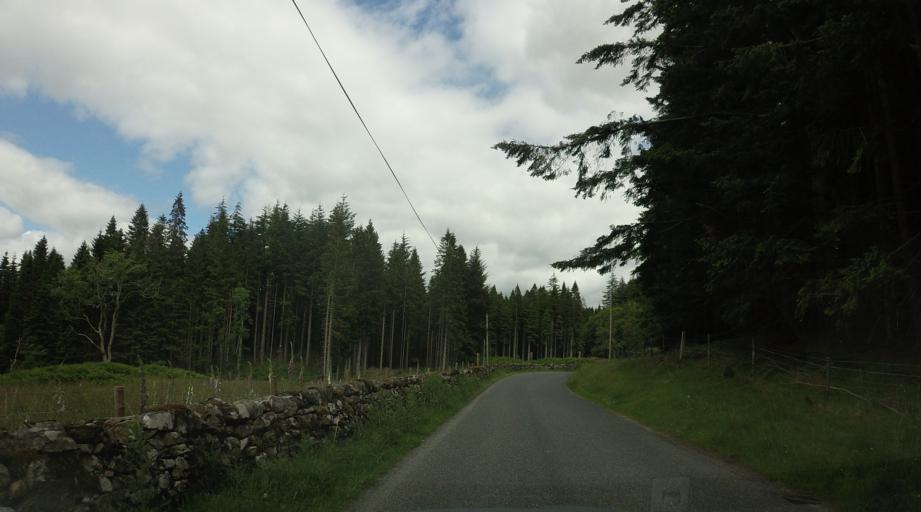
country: GB
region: Scotland
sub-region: Perth and Kinross
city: Aberfeldy
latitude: 56.6935
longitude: -4.1208
